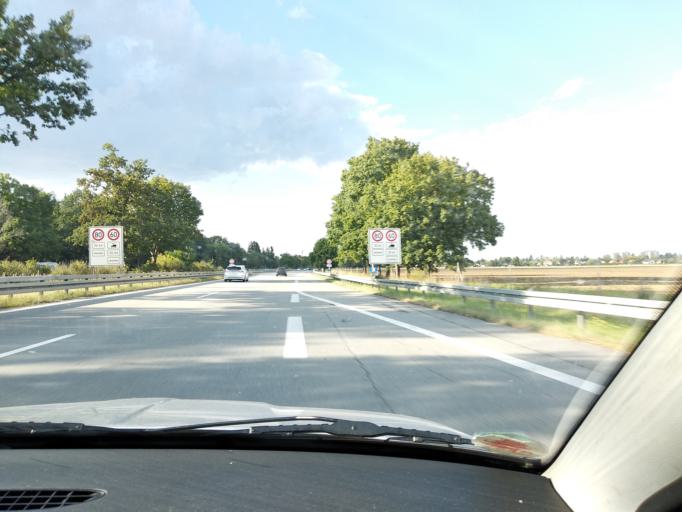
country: DE
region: Bavaria
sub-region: Upper Bavaria
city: Unterhaching
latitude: 48.0590
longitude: 11.5952
